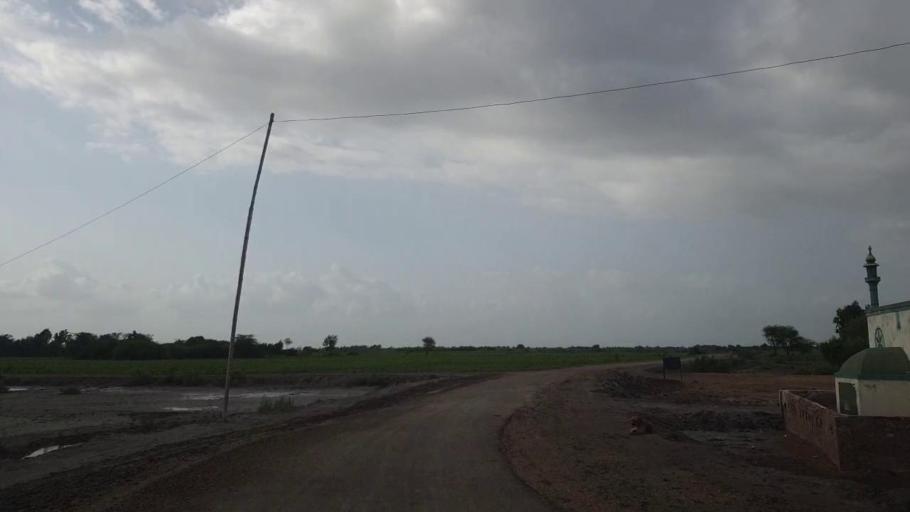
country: PK
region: Sindh
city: Kadhan
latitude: 24.5870
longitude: 69.0542
